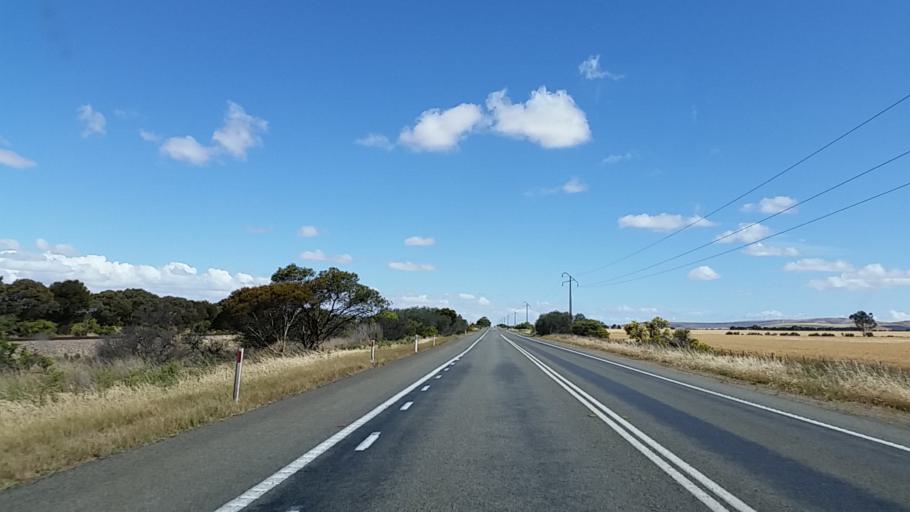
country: AU
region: South Australia
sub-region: Port Pirie City and Dists
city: Crystal Brook
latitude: -33.5671
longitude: 138.2247
